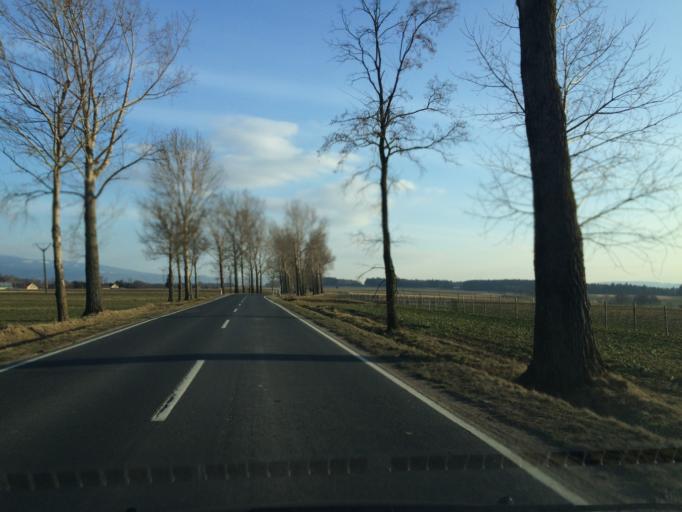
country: PL
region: Lower Silesian Voivodeship
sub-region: Powiat klodzki
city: Bystrzyca Klodzka
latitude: 50.2599
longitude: 16.6618
